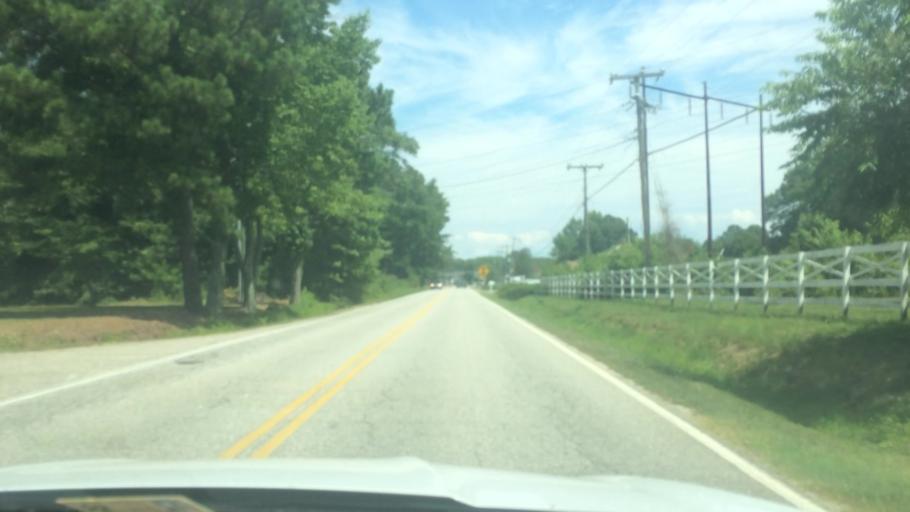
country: US
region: Virginia
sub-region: City of Poquoson
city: Poquoson
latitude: 37.1186
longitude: -76.4319
